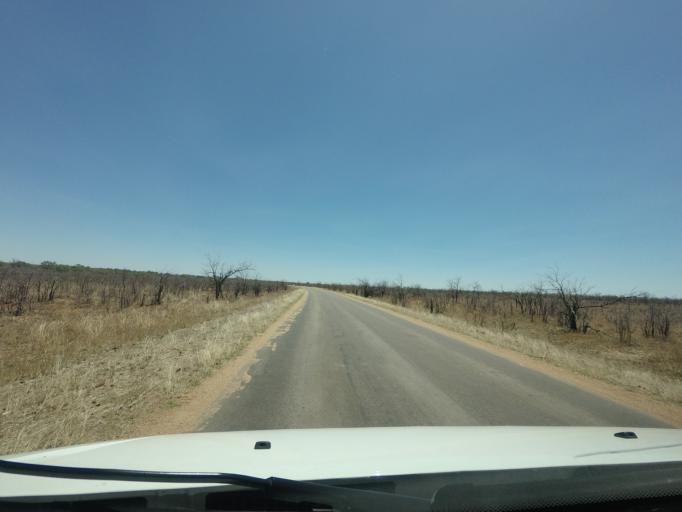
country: ZA
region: Limpopo
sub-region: Mopani District Municipality
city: Phalaborwa
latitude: -23.5602
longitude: 31.4509
